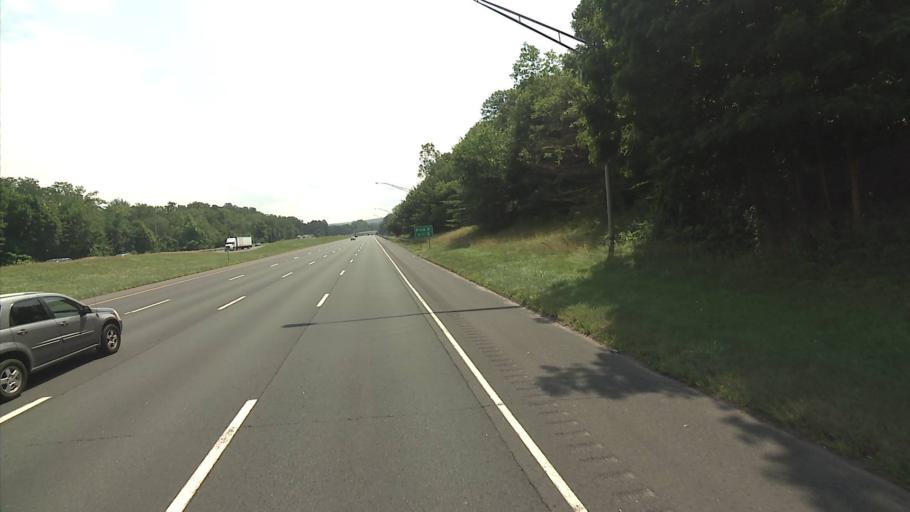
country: US
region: Connecticut
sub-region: Hartford County
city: Manchester
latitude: 41.7626
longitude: -72.5290
